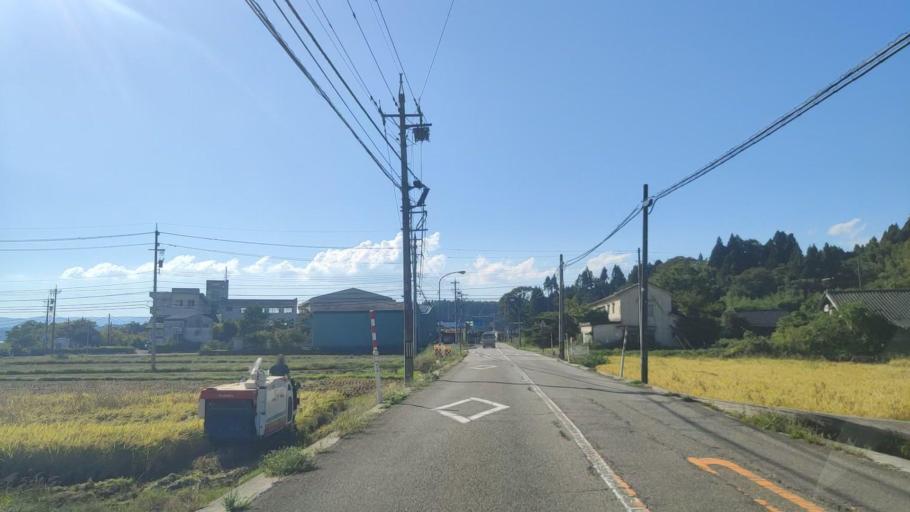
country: JP
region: Ishikawa
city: Nanao
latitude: 37.2345
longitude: 136.9693
